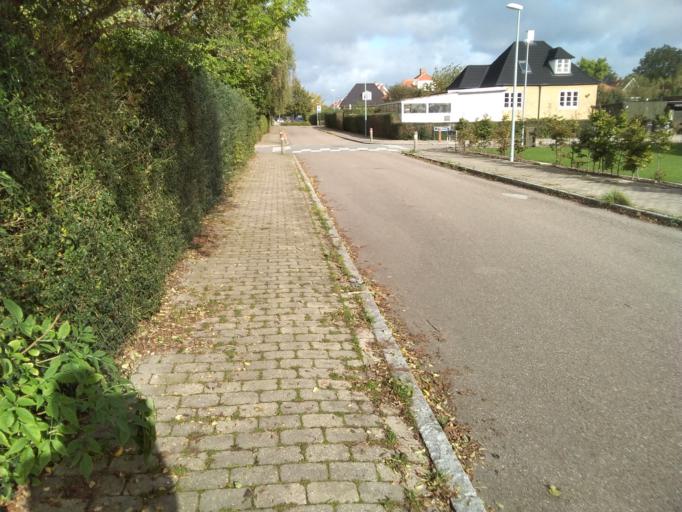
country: DK
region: Capital Region
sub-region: Tarnby Kommune
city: Tarnby
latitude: 55.6318
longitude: 12.6168
